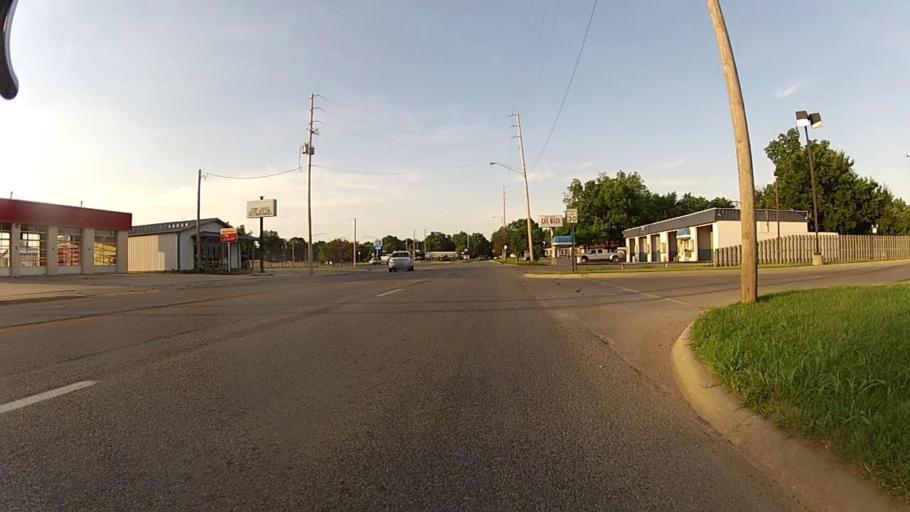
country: US
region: Kansas
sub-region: Cowley County
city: Arkansas City
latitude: 37.0793
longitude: -97.0401
